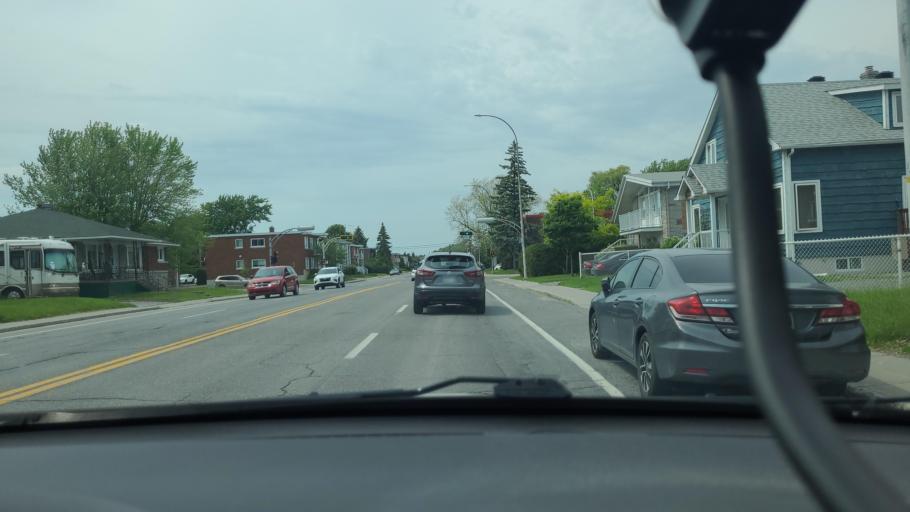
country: CA
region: Quebec
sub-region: Monteregie
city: Saint-Hyacinthe
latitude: 45.6279
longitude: -72.9658
